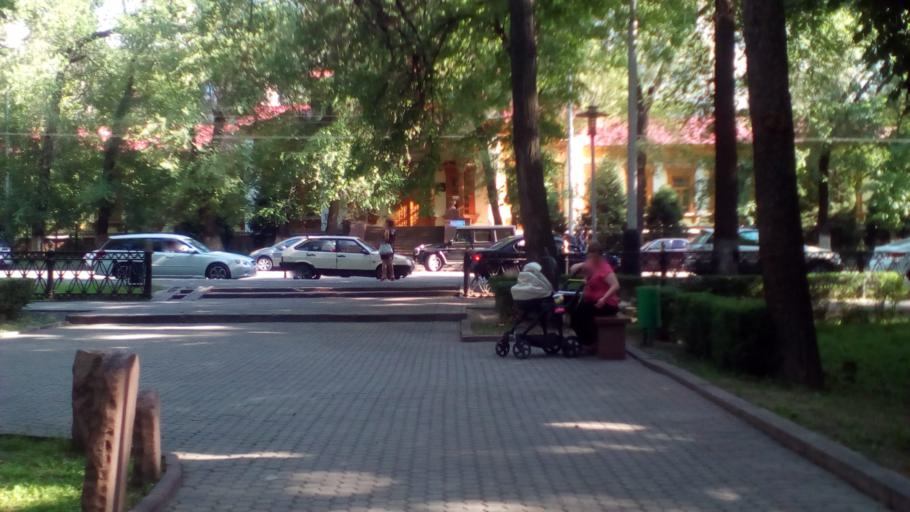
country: KZ
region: Almaty Qalasy
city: Almaty
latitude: 43.2494
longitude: 76.9360
